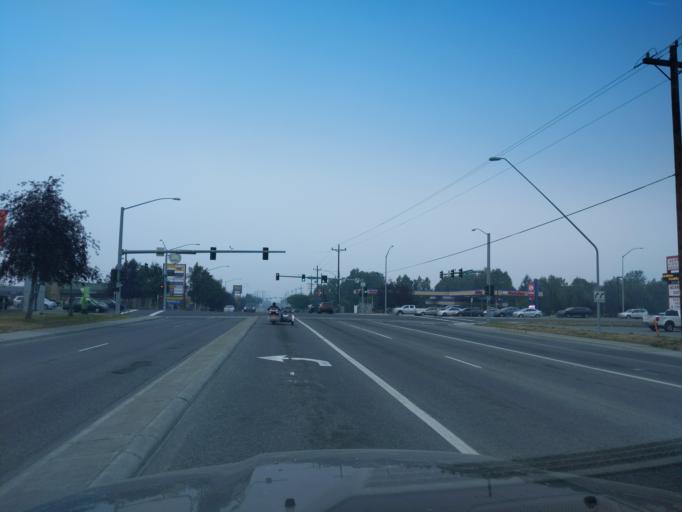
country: US
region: Alaska
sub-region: Anchorage Municipality
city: Anchorage
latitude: 61.1801
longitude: -149.8682
